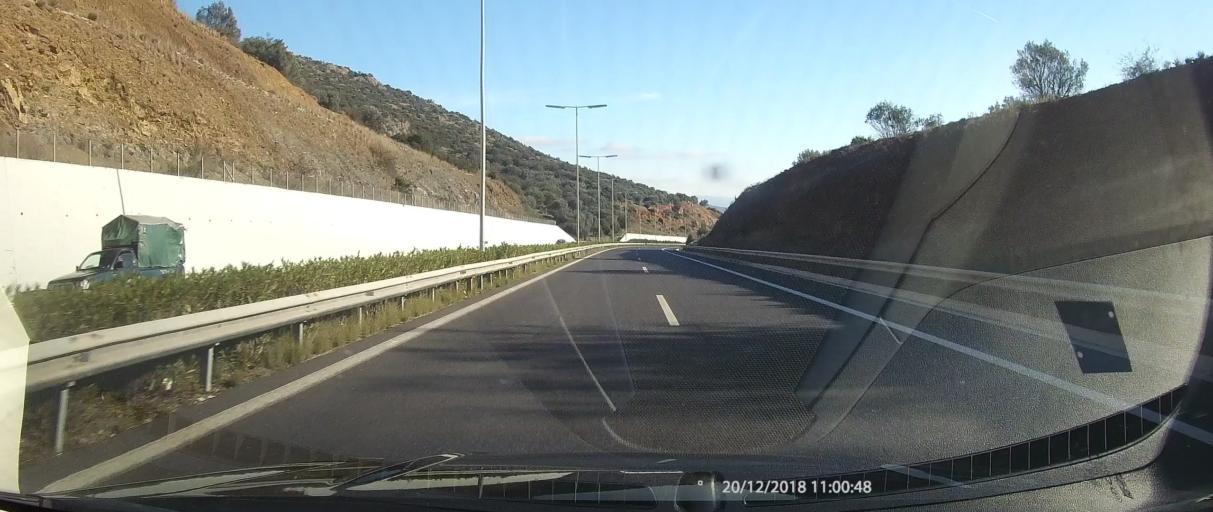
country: GR
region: Peloponnese
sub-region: Nomos Korinthias
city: Nemea
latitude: 37.7134
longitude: 22.5627
